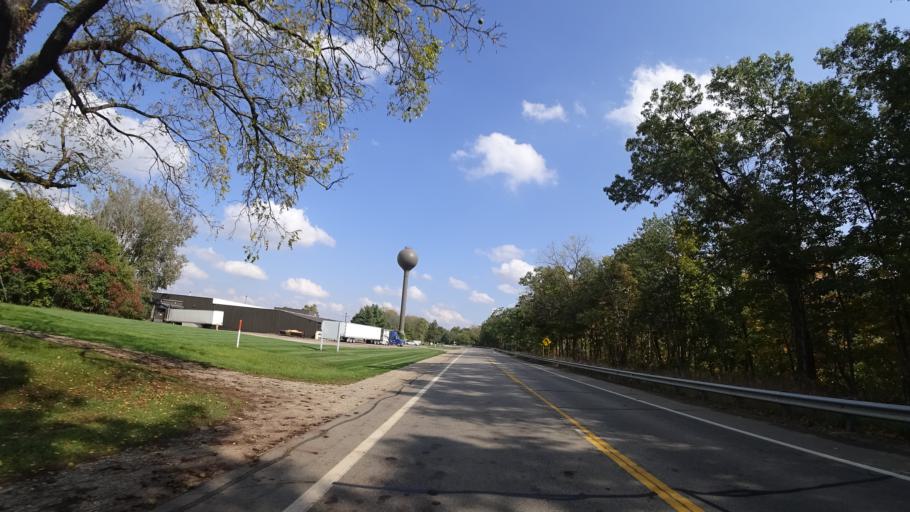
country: US
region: Michigan
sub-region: Saint Joseph County
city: Colon
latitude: 42.0073
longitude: -85.4326
